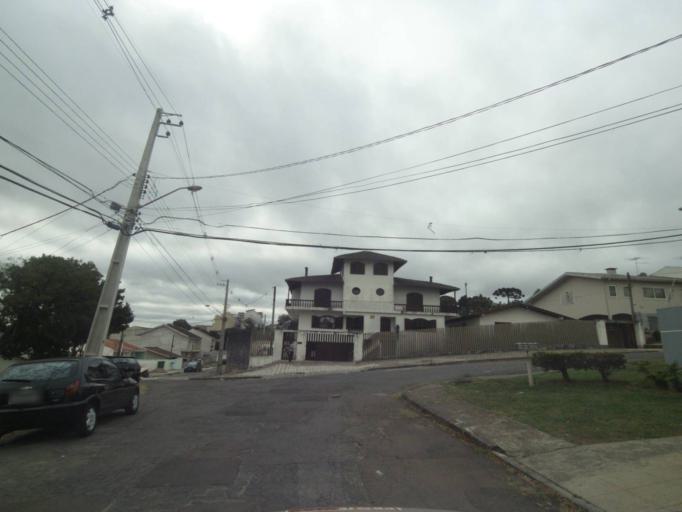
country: BR
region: Parana
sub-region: Sao Jose Dos Pinhais
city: Sao Jose dos Pinhais
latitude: -25.4858
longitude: -49.2314
